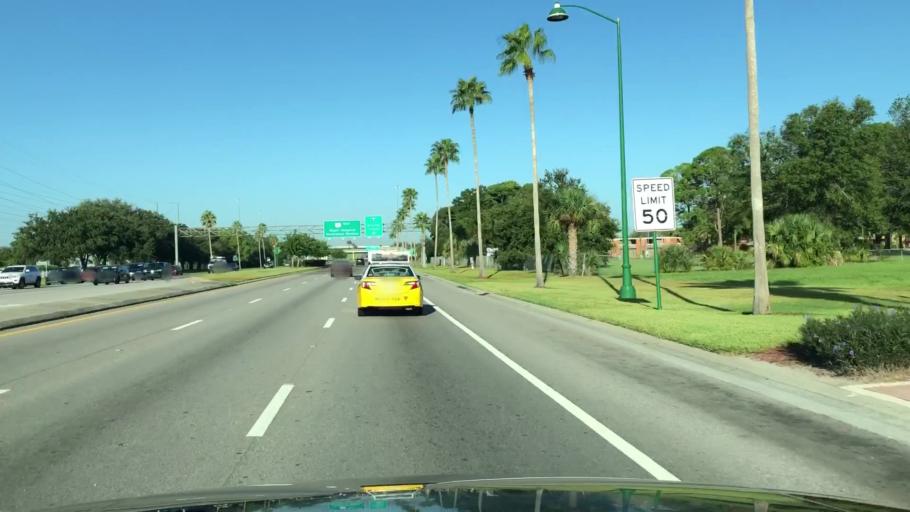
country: US
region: Florida
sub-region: Osceola County
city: Celebration
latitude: 28.3329
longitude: -81.5354
